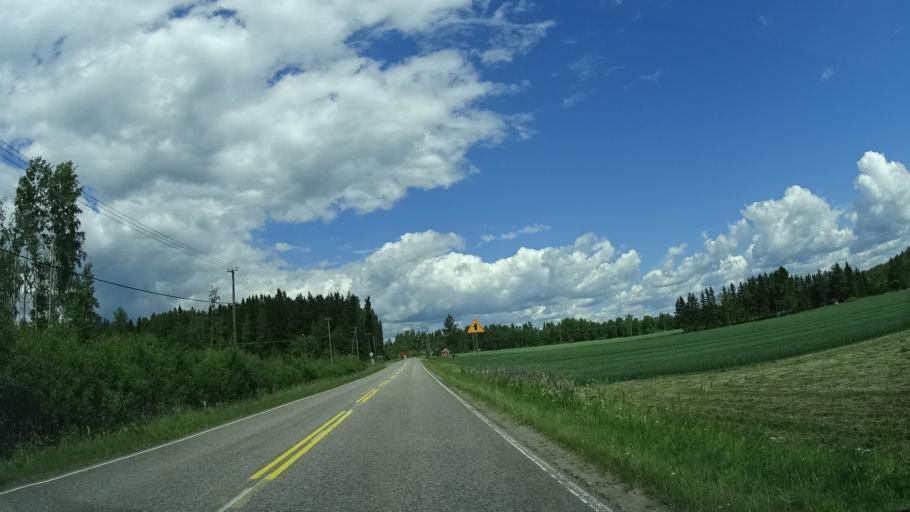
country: FI
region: Uusimaa
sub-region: Helsinki
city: Espoo
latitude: 60.3700
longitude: 24.6412
